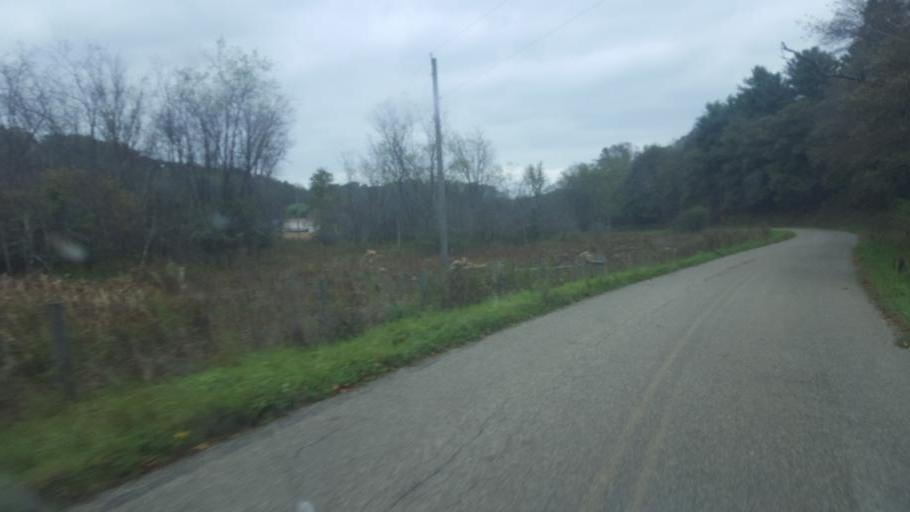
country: US
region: Ohio
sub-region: Harrison County
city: Cadiz
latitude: 40.4196
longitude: -81.0382
